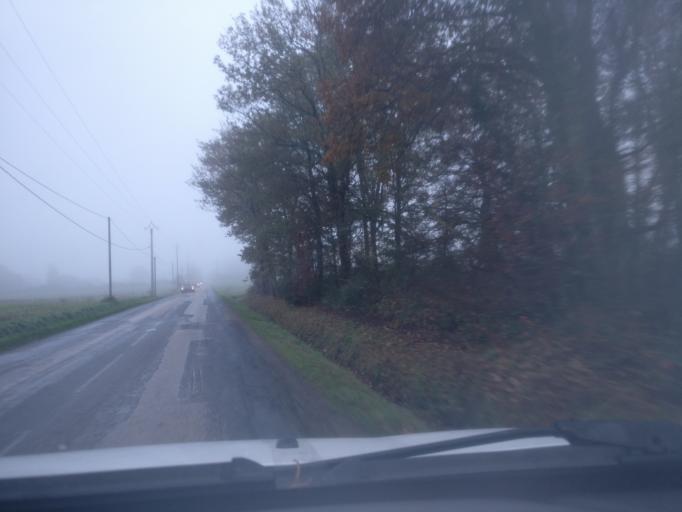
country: FR
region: Brittany
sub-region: Departement d'Ille-et-Vilaine
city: Laille
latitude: 47.9967
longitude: -1.7296
